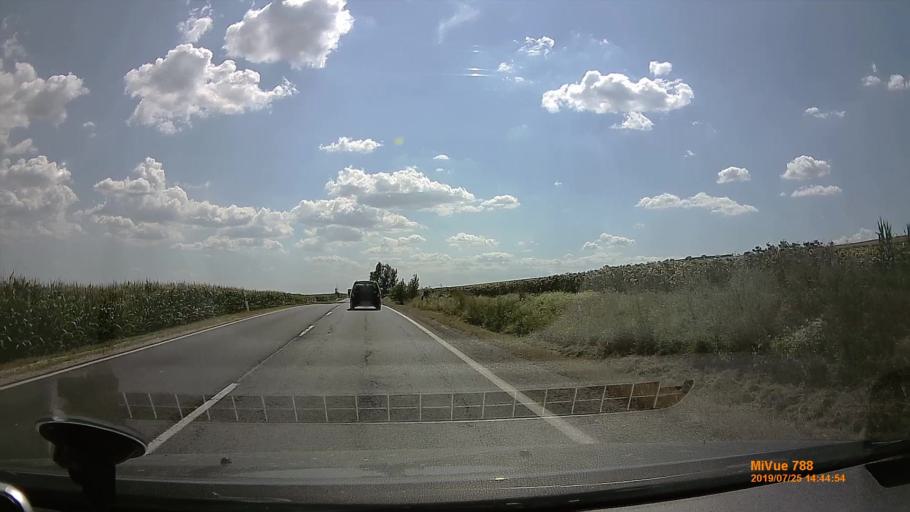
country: HU
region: Borsod-Abauj-Zemplen
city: Halmaj
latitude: 48.2652
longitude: 20.9961
